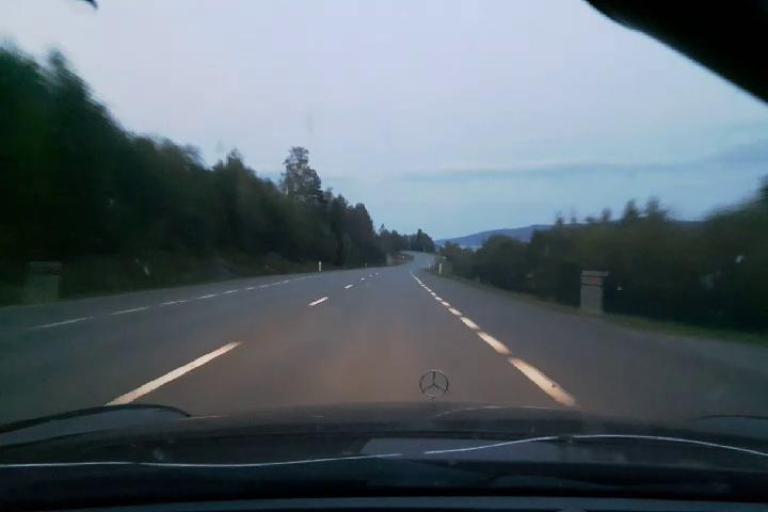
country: SE
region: Vaesternorrland
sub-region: Kramfors Kommun
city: Nordingra
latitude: 63.0045
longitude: 18.2557
